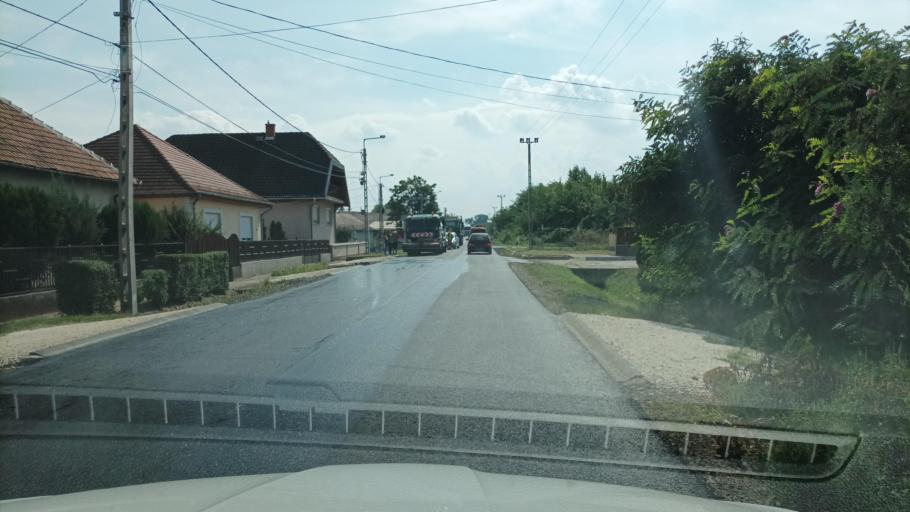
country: HU
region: Pest
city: Tura
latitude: 47.5942
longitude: 19.6045
